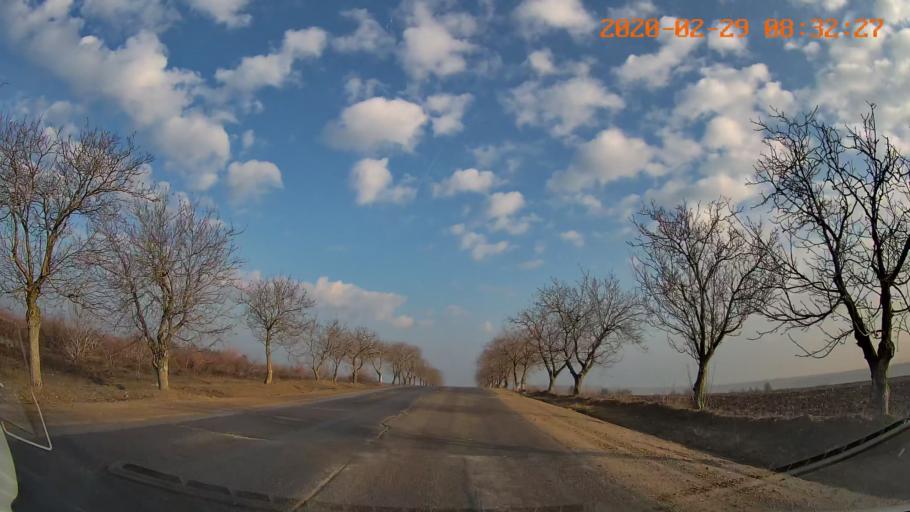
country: MD
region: Anenii Noi
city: Anenii Noi
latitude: 46.9251
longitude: 29.2872
